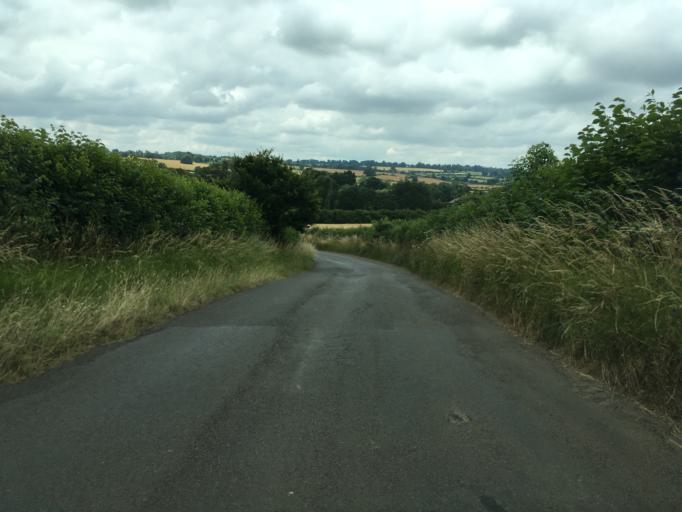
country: GB
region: England
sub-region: Oxfordshire
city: Bloxham
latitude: 51.9713
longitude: -1.3786
